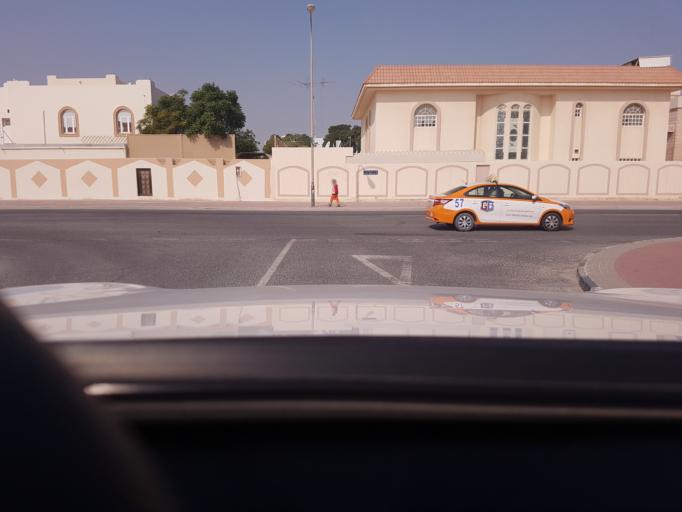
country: QA
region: Baladiyat ad Dawhah
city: Doha
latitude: 25.2374
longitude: 51.5616
